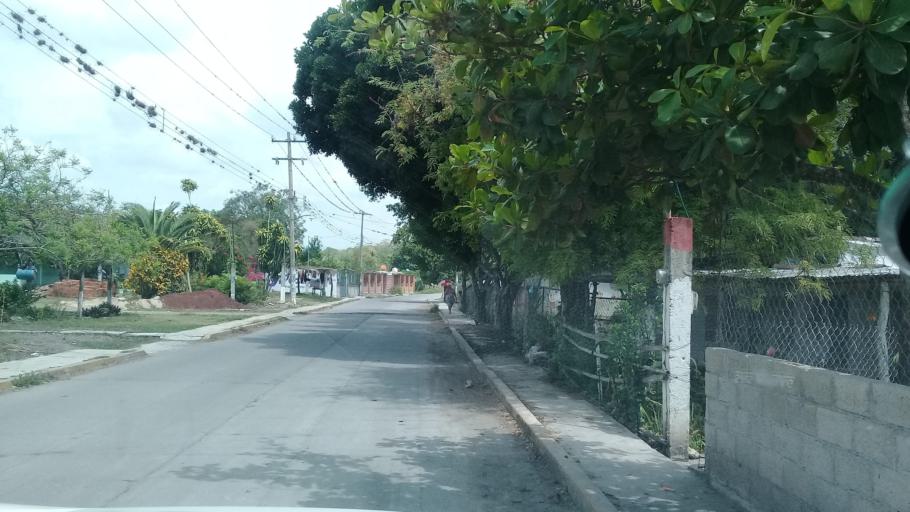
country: MX
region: Veracruz
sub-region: Emiliano Zapata
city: Plan del Rio
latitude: 19.3529
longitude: -96.6459
